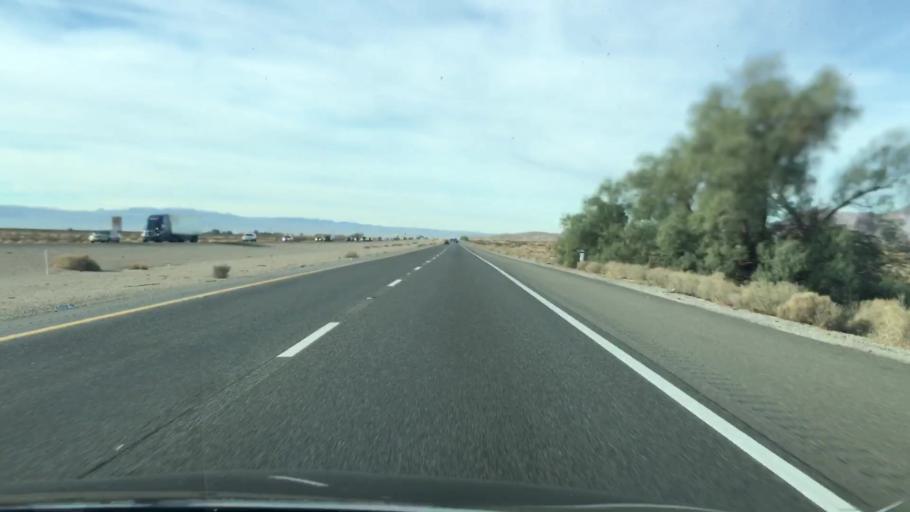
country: US
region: California
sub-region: San Bernardino County
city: Fort Irwin
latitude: 34.9461
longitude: -116.6859
